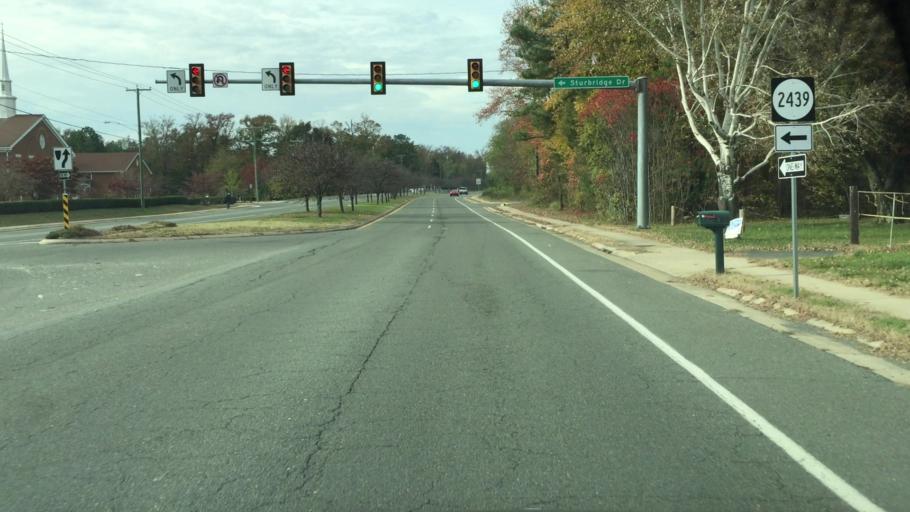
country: US
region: Virginia
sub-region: Chesterfield County
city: Bon Air
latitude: 37.5090
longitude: -77.5848
